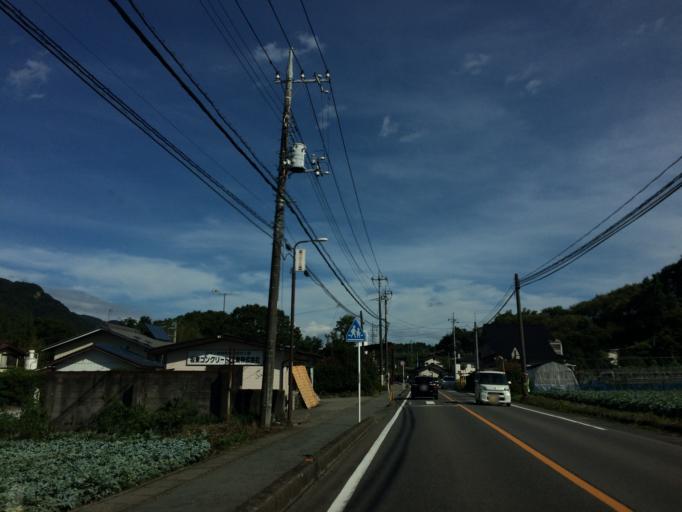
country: JP
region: Gunma
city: Nakanojomachi
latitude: 36.5666
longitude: 138.8769
